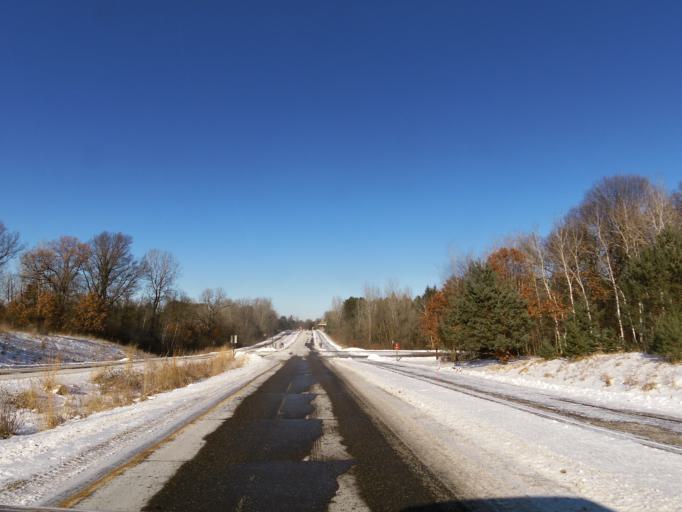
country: US
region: Minnesota
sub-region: Washington County
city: Lake Elmo
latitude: 44.9677
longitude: -92.9033
